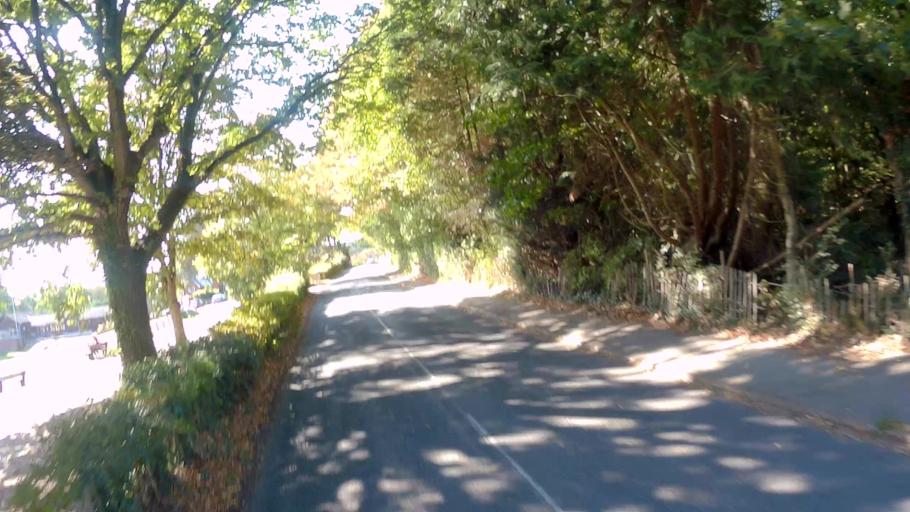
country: GB
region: England
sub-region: Surrey
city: Churt
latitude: 51.1732
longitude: -0.7924
